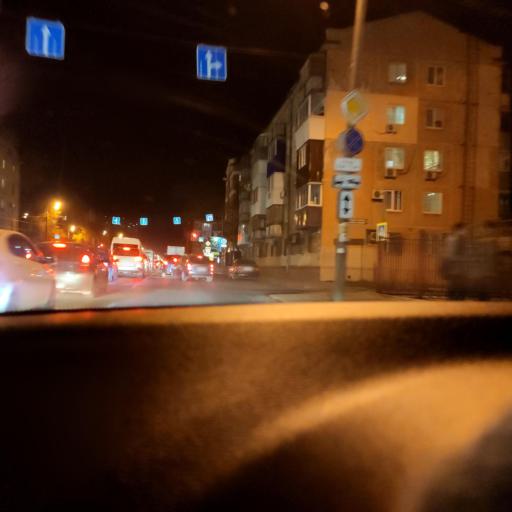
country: RU
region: Samara
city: Samara
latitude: 53.1994
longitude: 50.1904
